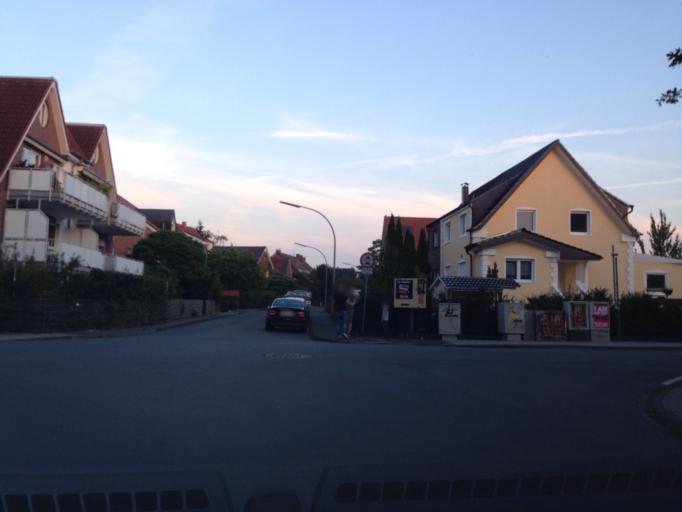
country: DE
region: North Rhine-Westphalia
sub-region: Regierungsbezirk Munster
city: Muenster
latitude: 51.9077
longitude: 7.6278
